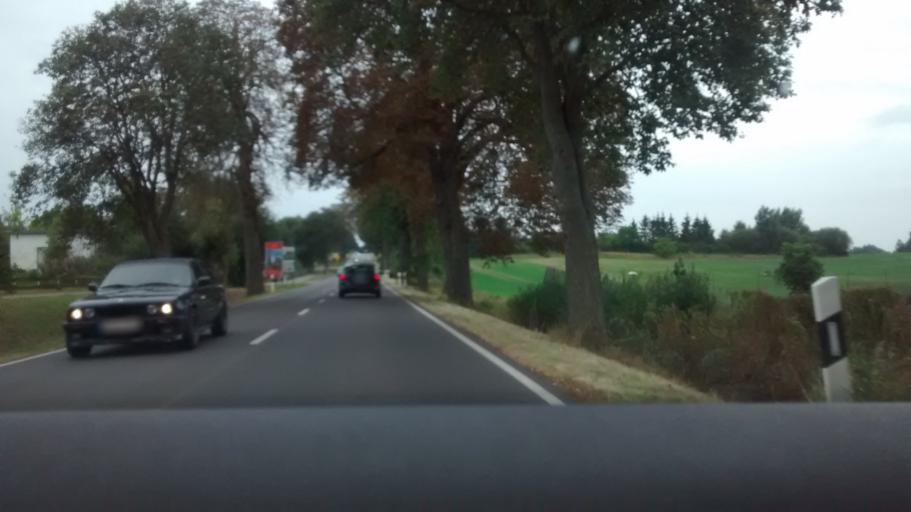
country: DE
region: Mecklenburg-Vorpommern
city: Mecklenburg
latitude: 53.8502
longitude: 11.4572
